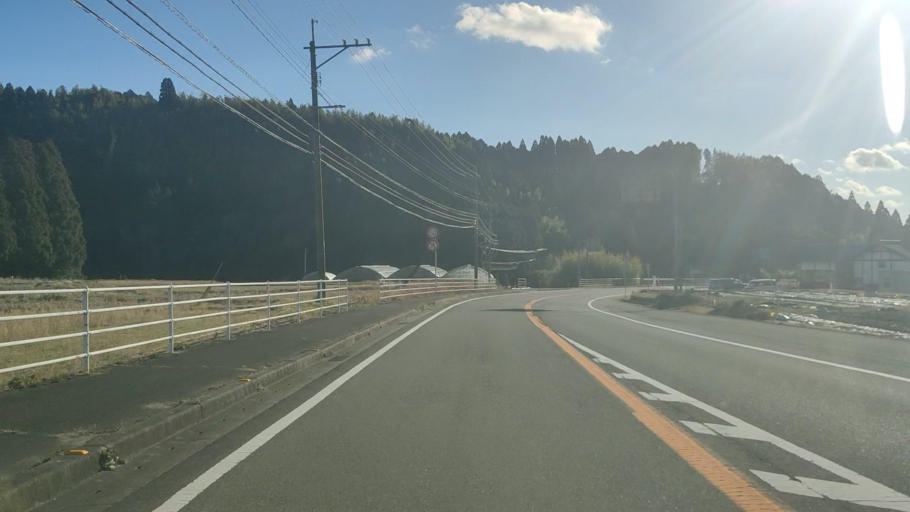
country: JP
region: Fukuoka
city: Maebaru-chuo
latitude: 33.4512
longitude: 130.2758
